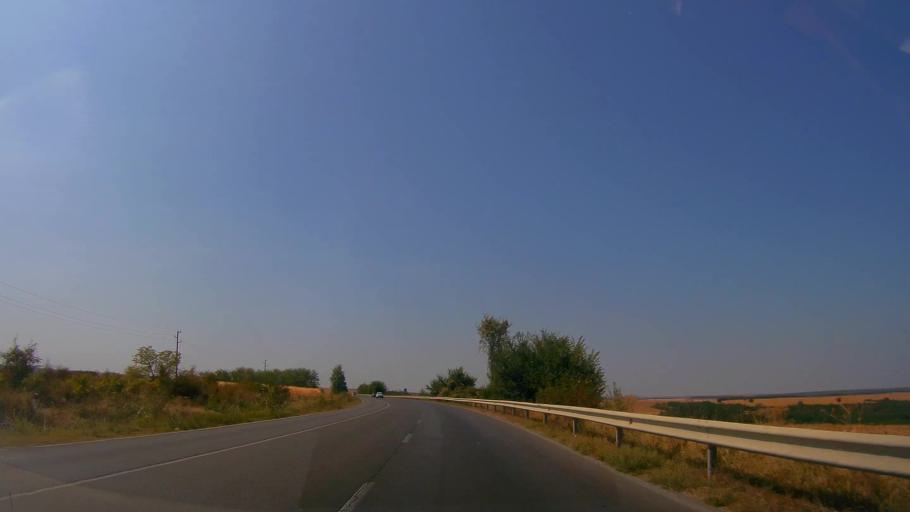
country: BG
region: Ruse
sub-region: Obshtina Vetovo
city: Senovo
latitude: 43.5619
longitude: 26.3608
